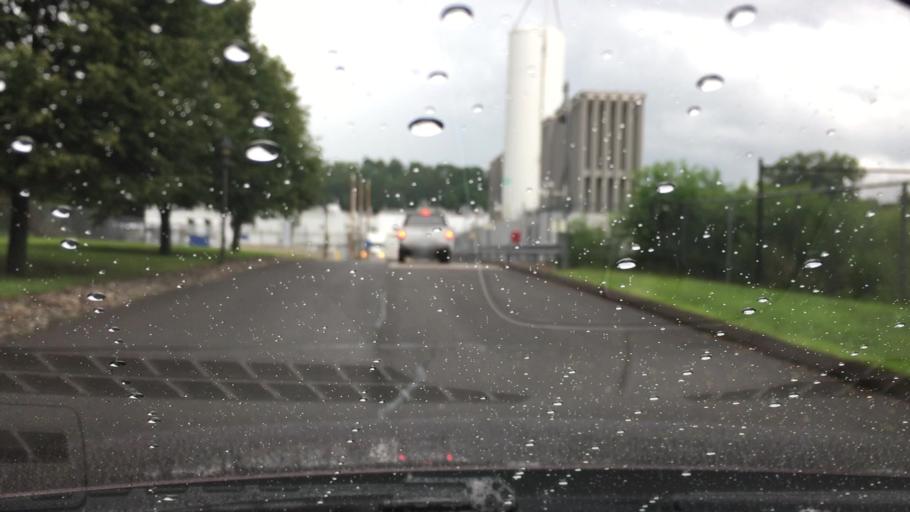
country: US
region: Connecticut
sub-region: Hartford County
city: South Windsor
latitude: 41.8317
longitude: -72.6095
